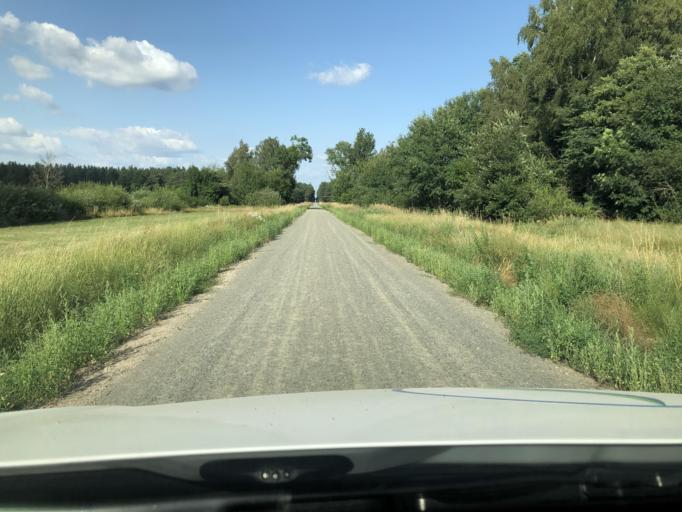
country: SE
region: Skane
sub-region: Kristianstads Kommun
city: Norra Asum
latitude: 55.9120
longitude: 14.1140
